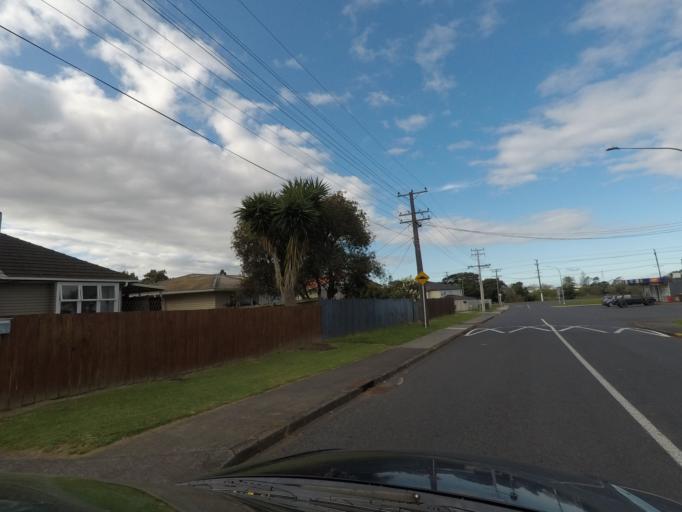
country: NZ
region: Auckland
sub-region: Auckland
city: Rosebank
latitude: -36.8842
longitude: 174.6565
